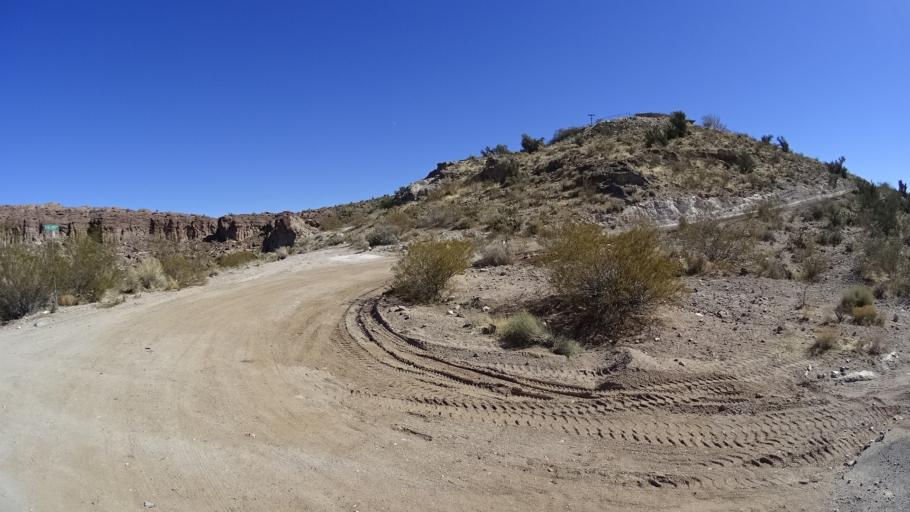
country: US
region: Arizona
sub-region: Mohave County
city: Kingman
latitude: 35.1990
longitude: -114.0571
